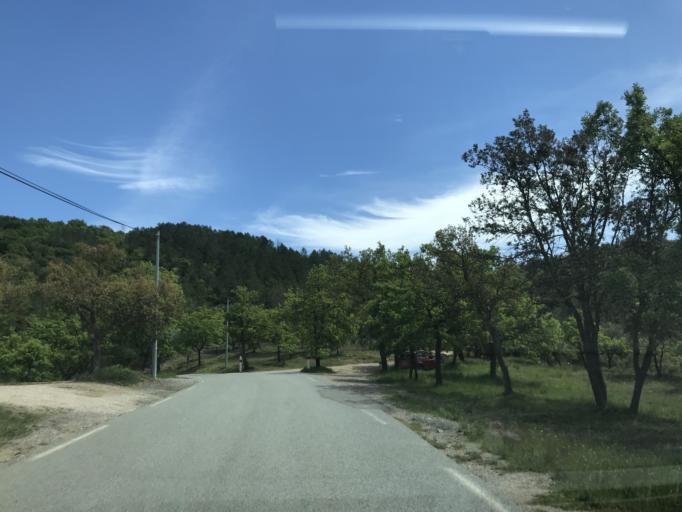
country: FR
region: Provence-Alpes-Cote d'Azur
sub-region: Departement du Var
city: Montauroux
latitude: 43.5835
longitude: 6.8135
